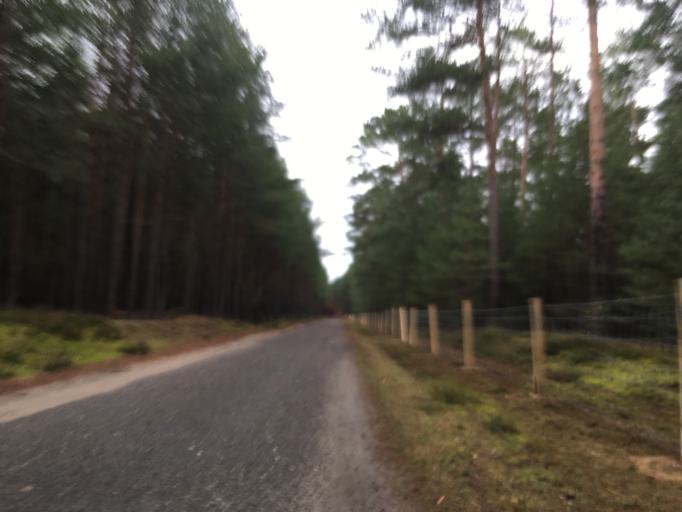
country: DE
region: Brandenburg
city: Jamlitz
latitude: 52.0608
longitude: 14.4811
